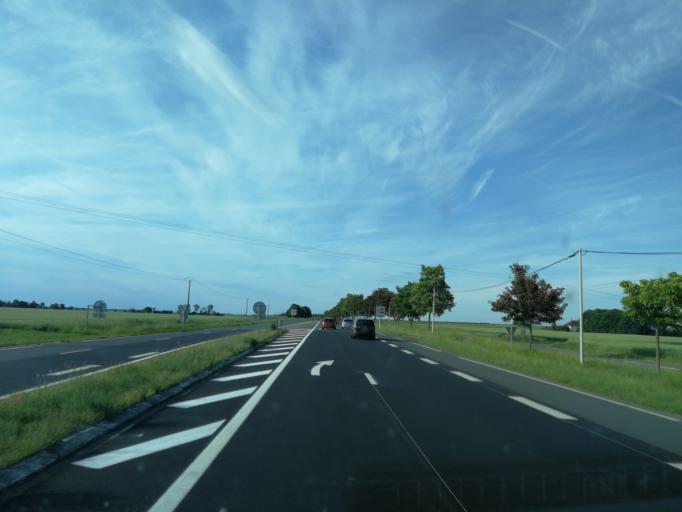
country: FR
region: Centre
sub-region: Departement d'Eure-et-Loir
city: Bonneval
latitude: 48.2068
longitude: 1.3981
